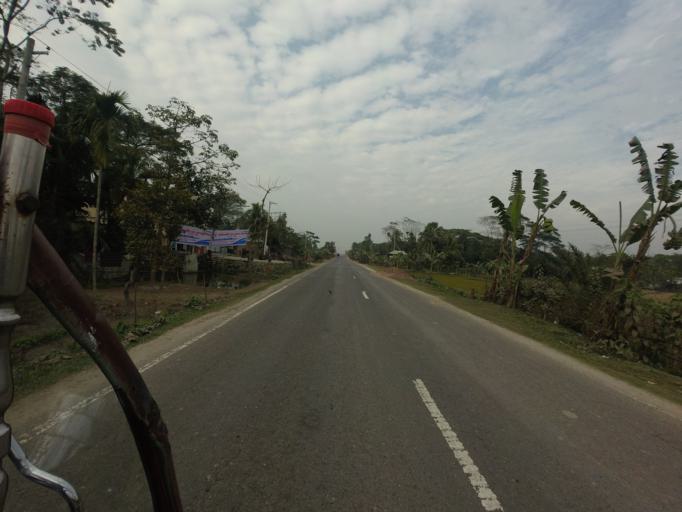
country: BD
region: Barisal
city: Nalchiti
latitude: 22.4552
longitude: 90.3408
